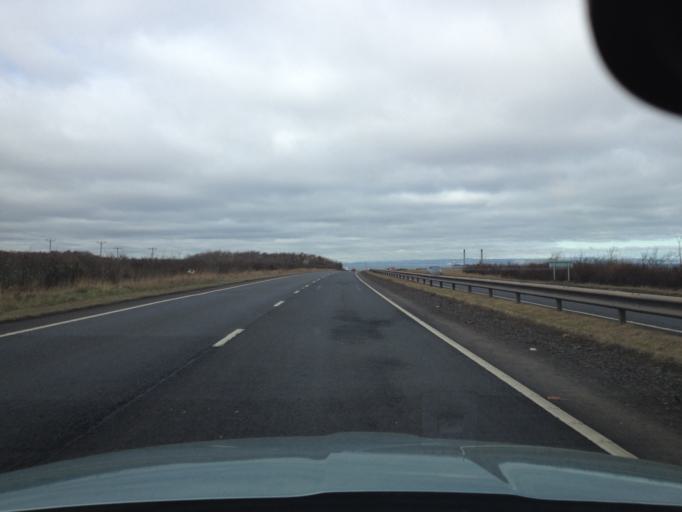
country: GB
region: Scotland
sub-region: East Lothian
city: Macmerry
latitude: 55.9486
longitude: -2.9182
